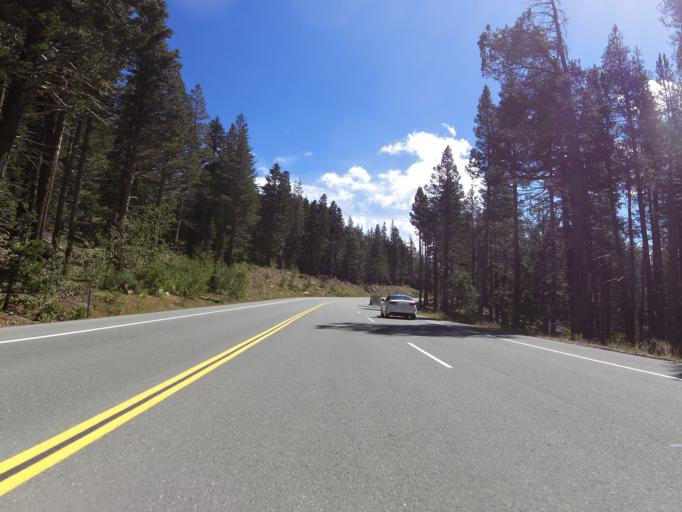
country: US
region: California
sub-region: El Dorado County
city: South Lake Tahoe
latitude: 38.6963
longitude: -120.0013
